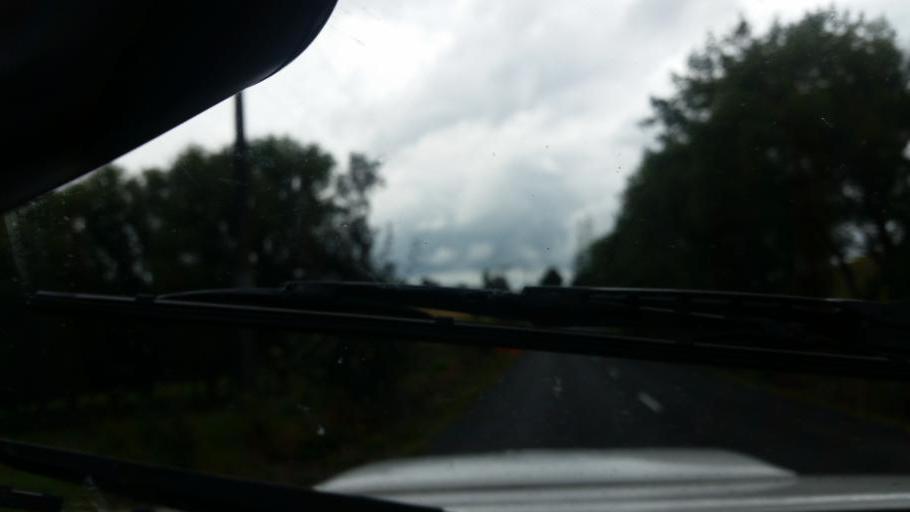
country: NZ
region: Auckland
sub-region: Auckland
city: Wellsford
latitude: -36.1475
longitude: 174.2226
